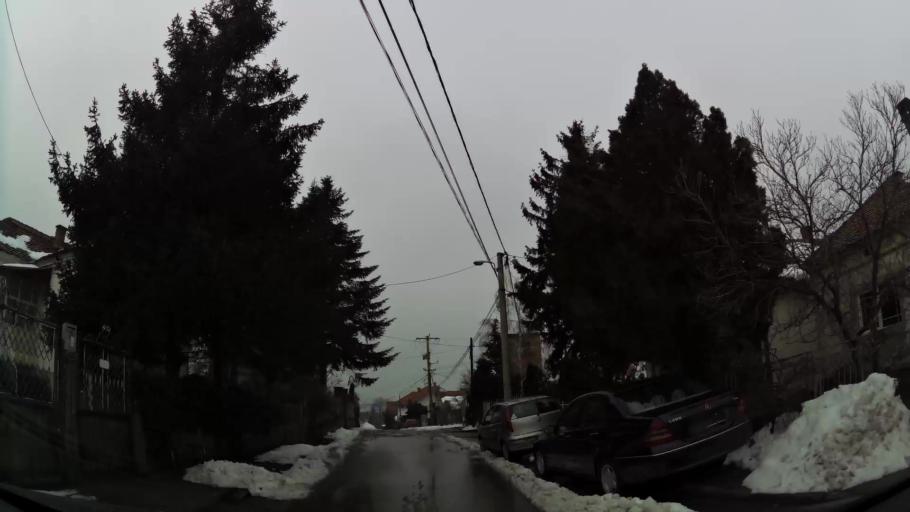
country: RS
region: Central Serbia
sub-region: Belgrade
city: Zvezdara
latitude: 44.7597
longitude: 20.5271
